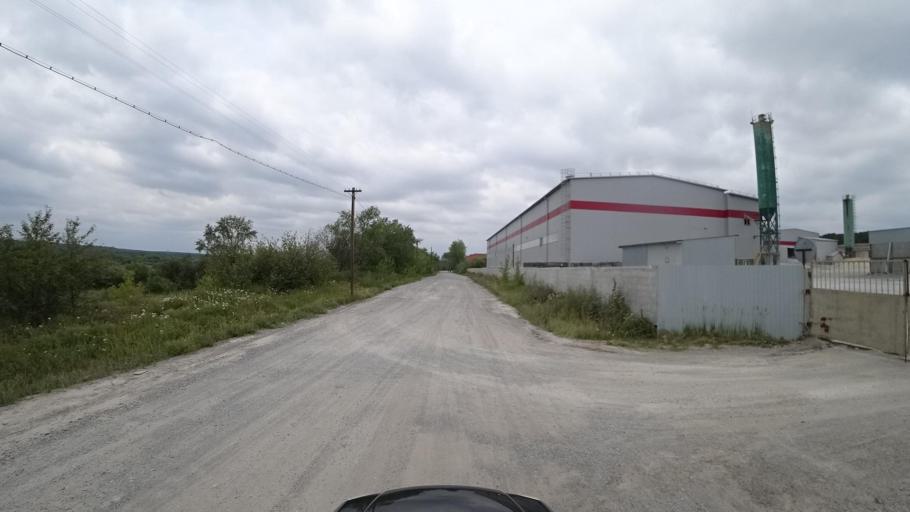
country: RU
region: Sverdlovsk
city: Kamyshlov
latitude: 56.8303
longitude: 62.7272
